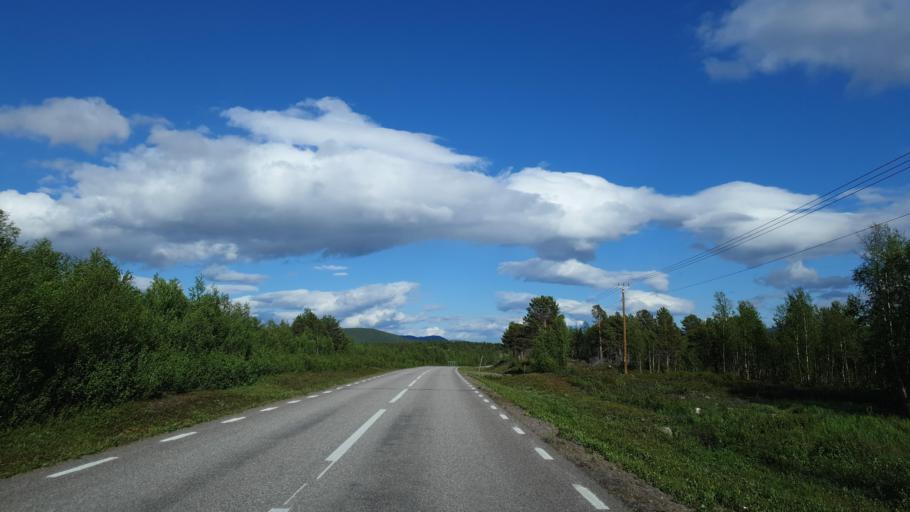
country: SE
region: Norrbotten
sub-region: Kiruna Kommun
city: Kiruna
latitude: 67.8749
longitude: 19.2043
